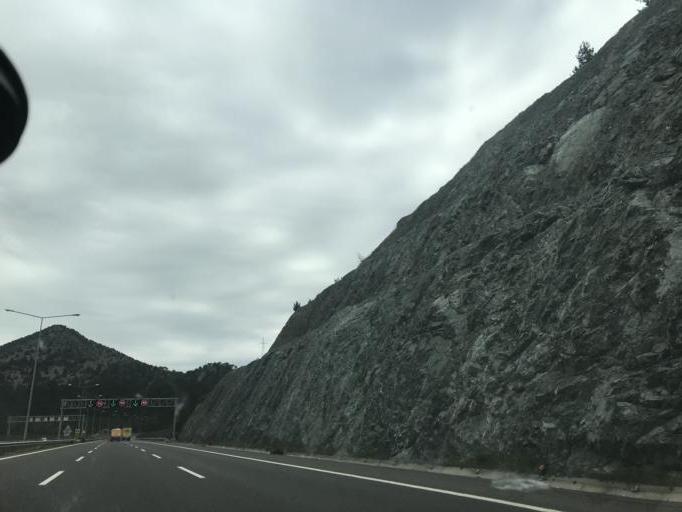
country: TR
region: Nigde
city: Ciftehan
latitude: 37.5014
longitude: 34.8249
